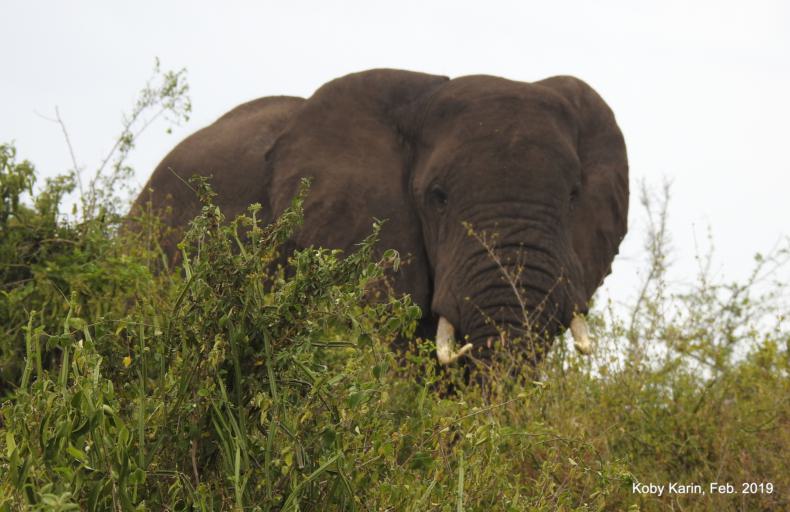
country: UG
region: Western Region
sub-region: Rubirizi District
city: Rubirizi
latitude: -0.1502
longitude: 29.9178
